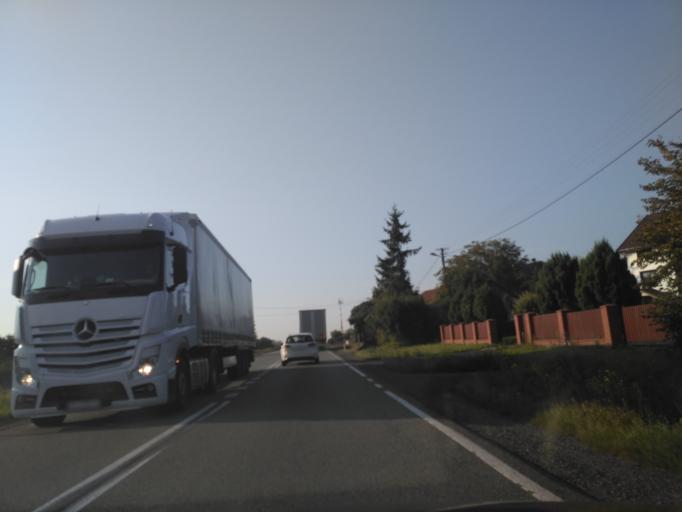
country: PL
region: Lublin Voivodeship
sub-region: Powiat krasnicki
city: Szastarka
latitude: 50.8234
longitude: 22.3145
